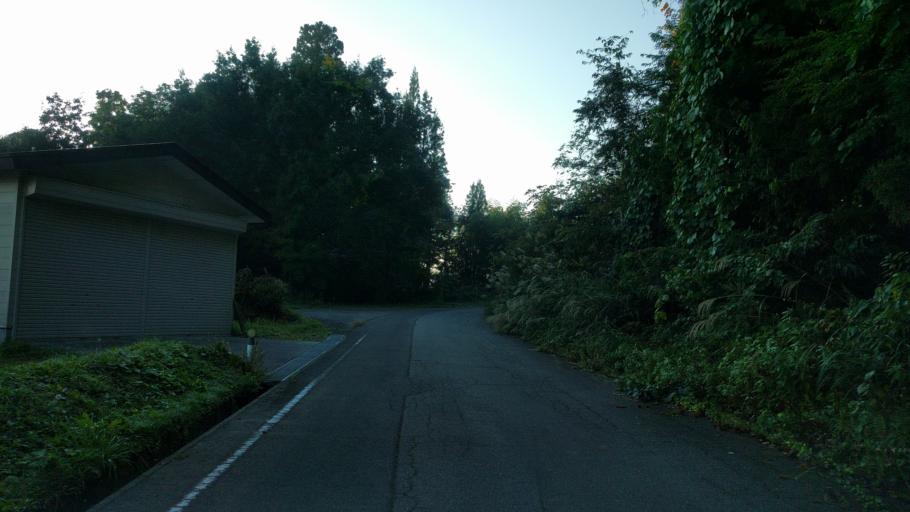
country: JP
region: Fukushima
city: Kitakata
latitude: 37.4321
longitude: 139.7991
